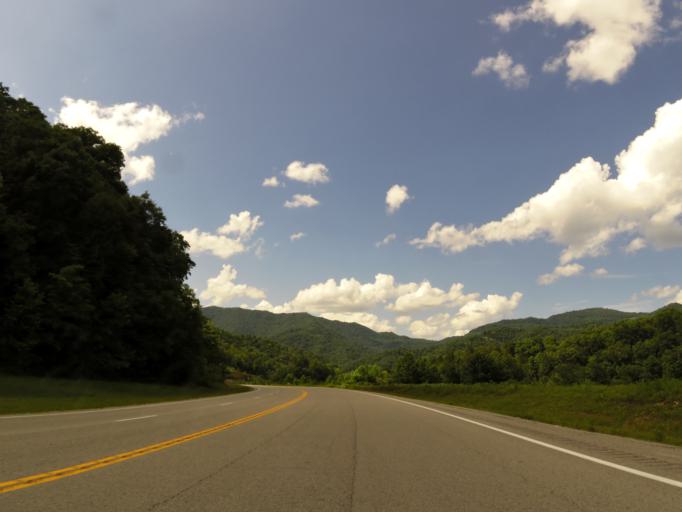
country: US
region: Kentucky
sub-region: Harlan County
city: Harlan
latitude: 36.7979
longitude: -83.2683
